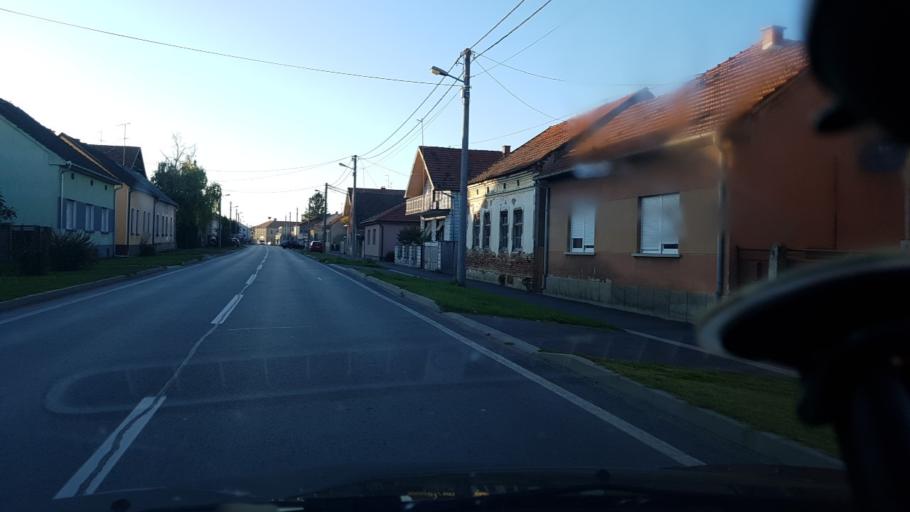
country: HR
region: Koprivnicko-Krizevacka
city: Virje
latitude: 46.0642
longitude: 16.9934
